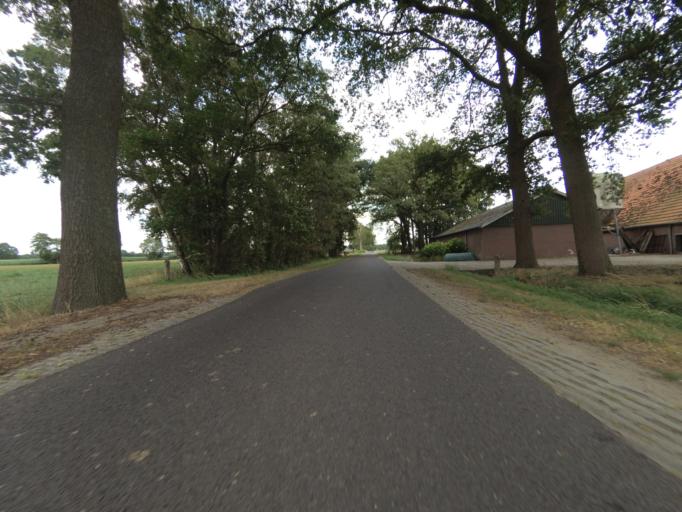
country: NL
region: Overijssel
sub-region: Gemeente Hof van Twente
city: Hengevelde
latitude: 52.1735
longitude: 6.6699
